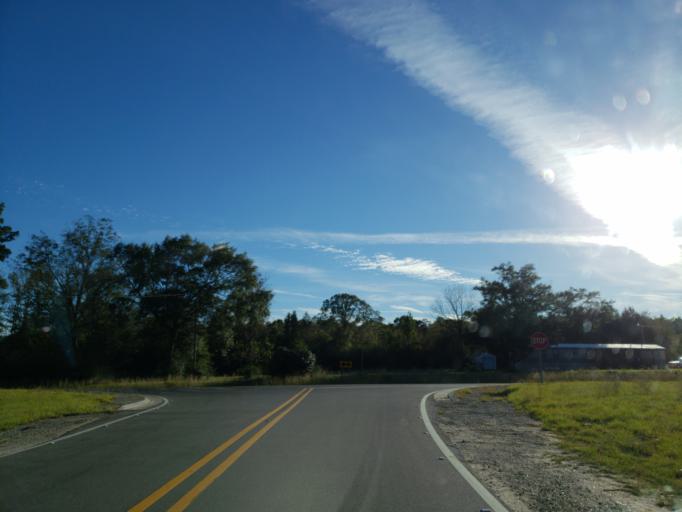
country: US
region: Mississippi
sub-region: Perry County
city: Richton
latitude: 31.3676
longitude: -88.8146
